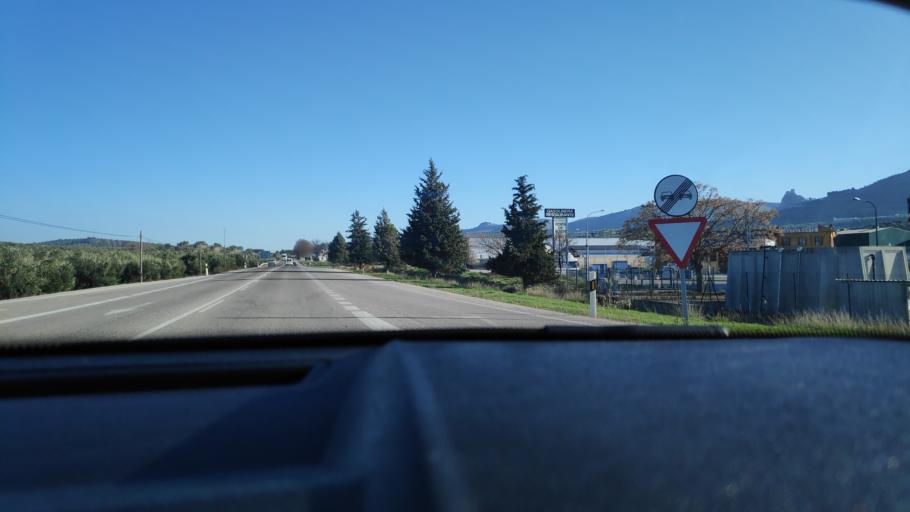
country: ES
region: Andalusia
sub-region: Province of Cordoba
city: Luque
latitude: 37.5818
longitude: -4.2849
